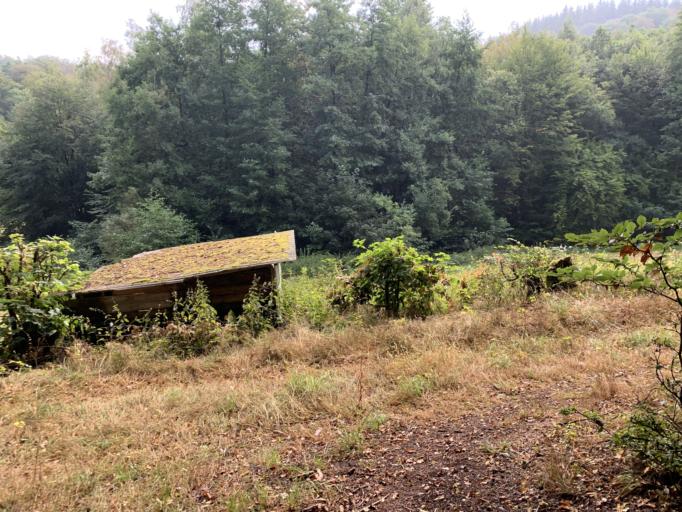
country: DE
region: Rheinland-Pfalz
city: Holzhausen an der Haide
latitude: 50.2191
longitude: 7.9214
